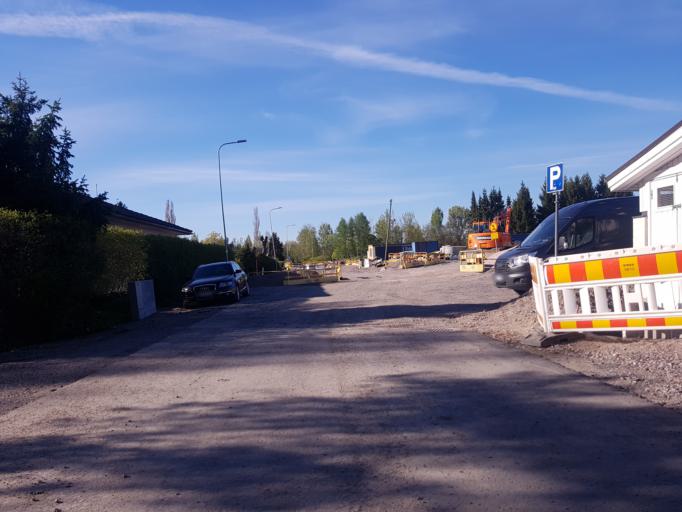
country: FI
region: Uusimaa
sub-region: Helsinki
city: Vantaa
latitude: 60.2720
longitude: 25.0253
